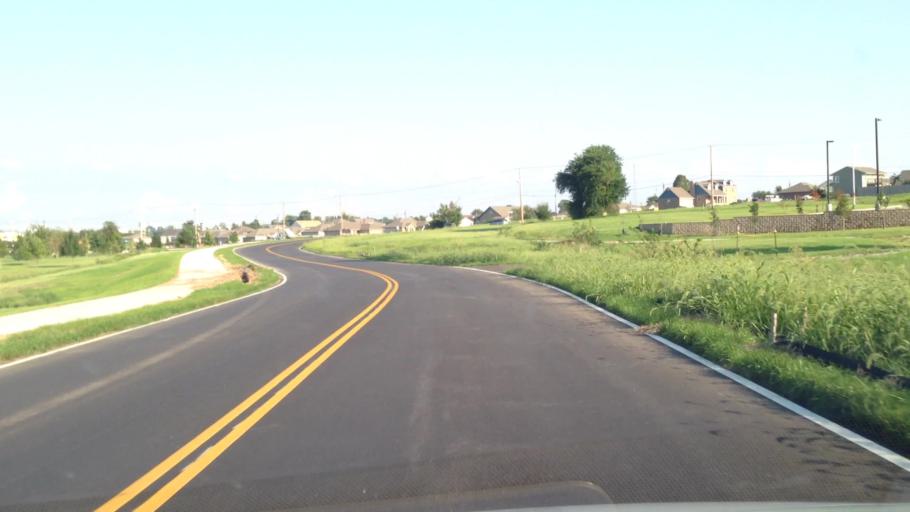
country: US
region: Missouri
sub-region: Jasper County
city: Duquesne
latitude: 37.0707
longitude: -94.4861
